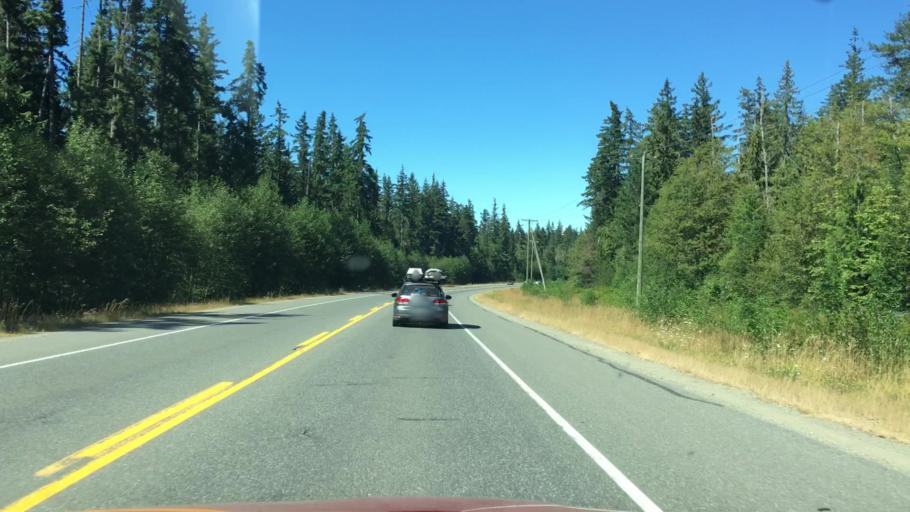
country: CA
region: British Columbia
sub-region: Regional District of Nanaimo
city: Parksville
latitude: 49.3085
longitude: -124.4500
